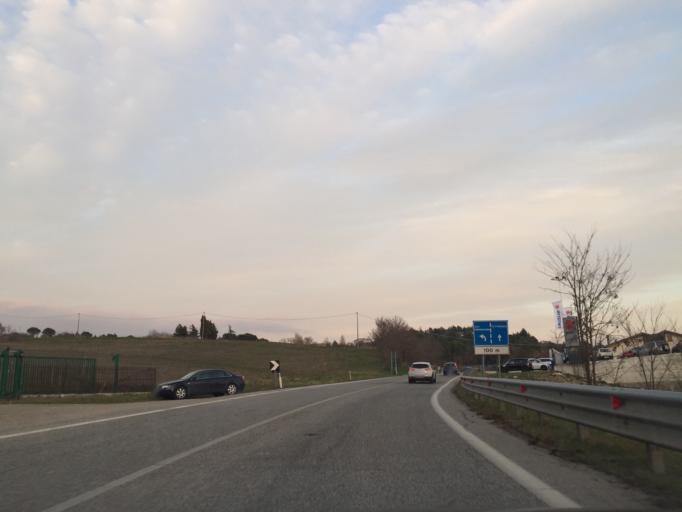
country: IT
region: Molise
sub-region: Provincia di Campobasso
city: Campodipietra
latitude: 41.5590
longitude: 14.7257
